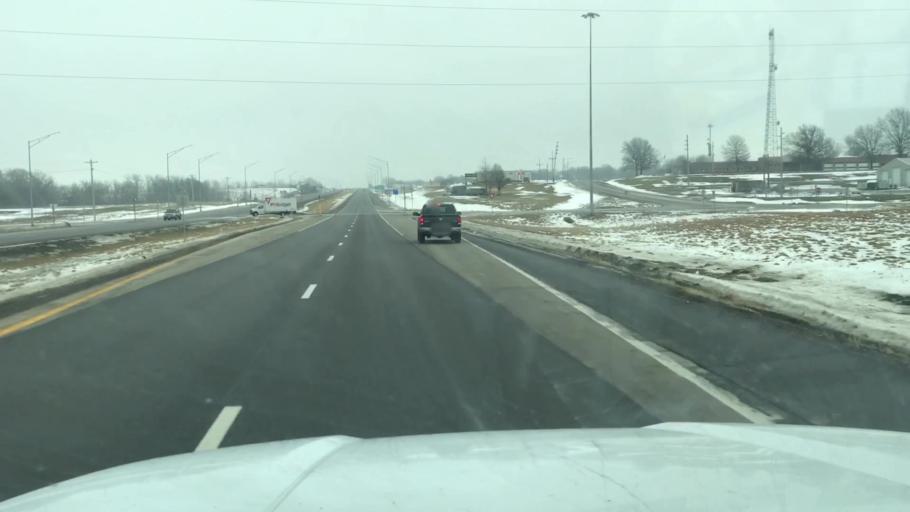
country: US
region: Missouri
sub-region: Clinton County
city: Cameron
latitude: 39.7539
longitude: -94.2539
